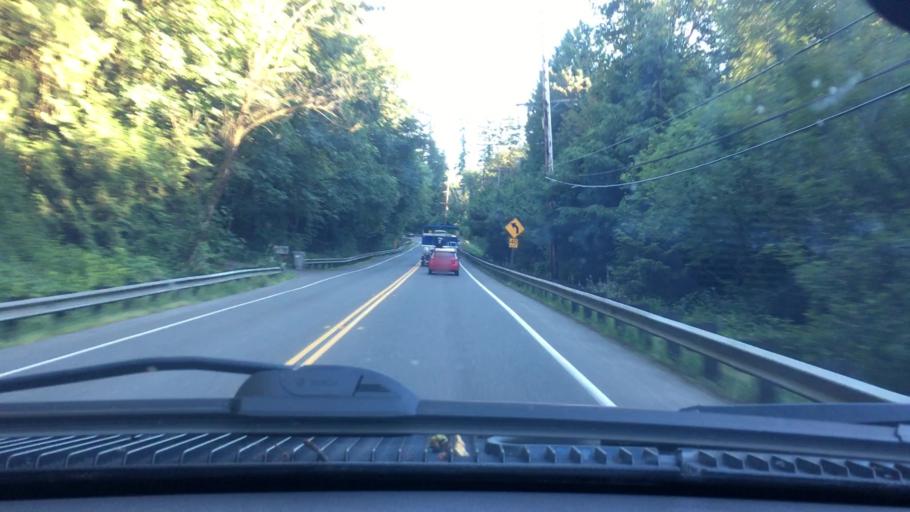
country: US
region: Washington
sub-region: King County
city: Mirrormont
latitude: 47.4814
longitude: -122.0286
